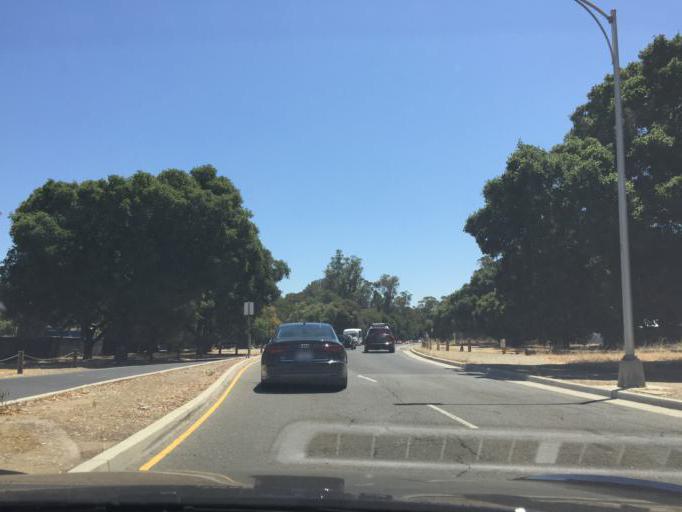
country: US
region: California
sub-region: Santa Clara County
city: Stanford
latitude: 37.4392
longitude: -122.1703
